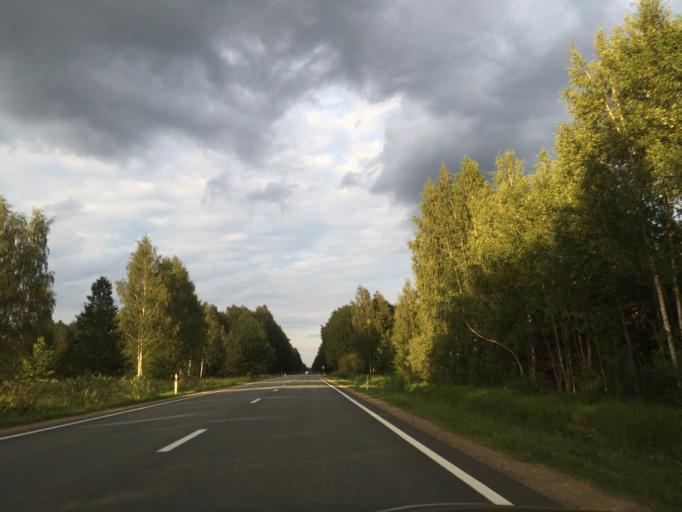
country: LV
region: Jurmala
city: Jurmala
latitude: 56.9160
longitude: 23.8068
